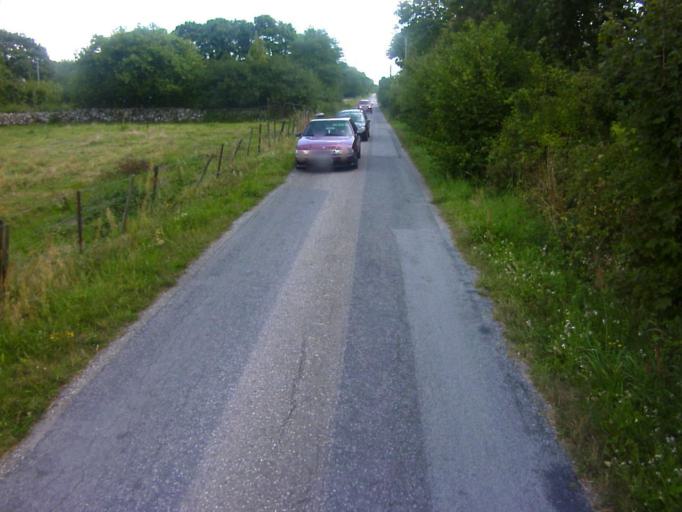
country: SE
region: Blekinge
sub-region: Solvesborgs Kommun
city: Soelvesborg
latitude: 56.0047
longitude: 14.6732
